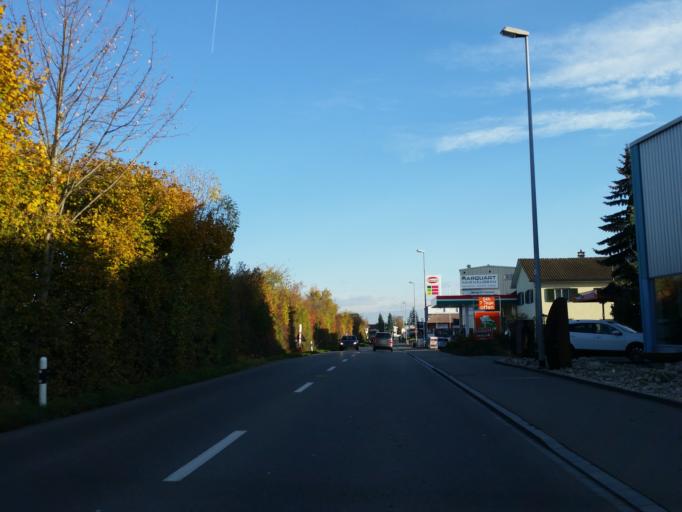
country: CH
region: Thurgau
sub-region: Arbon District
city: Uttwil
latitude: 47.5748
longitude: 9.3593
